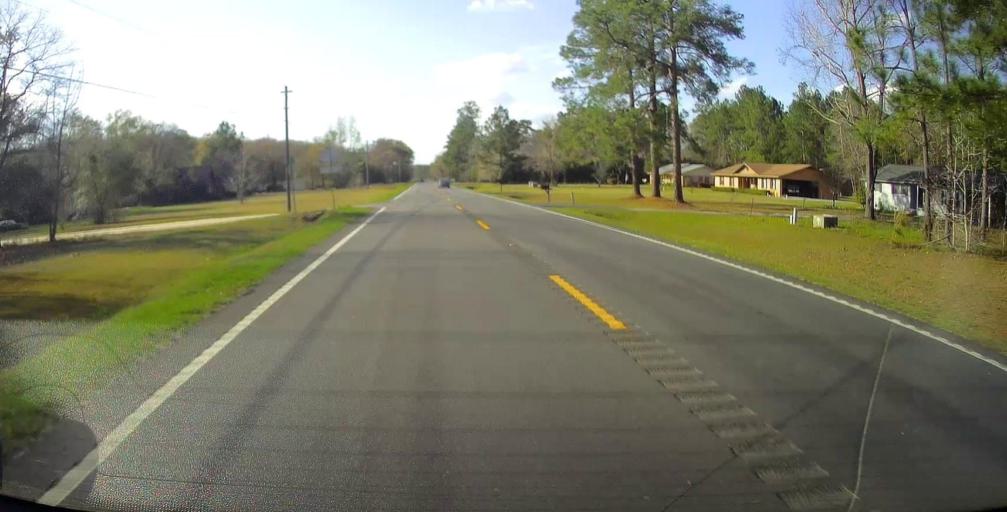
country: US
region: Georgia
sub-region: Montgomery County
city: Mount Vernon
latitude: 32.1852
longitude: -82.6081
